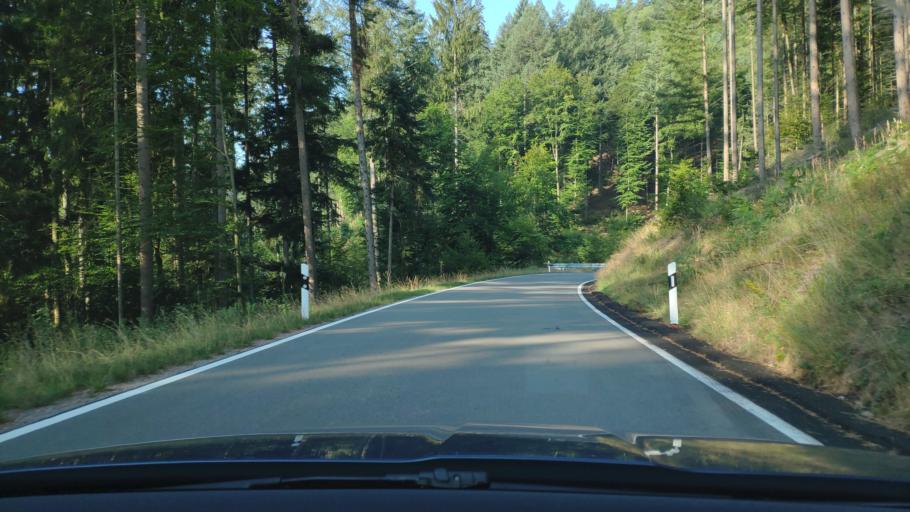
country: DE
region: Rheinland-Pfalz
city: Eppenbrunn
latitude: 49.0971
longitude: 7.6024
